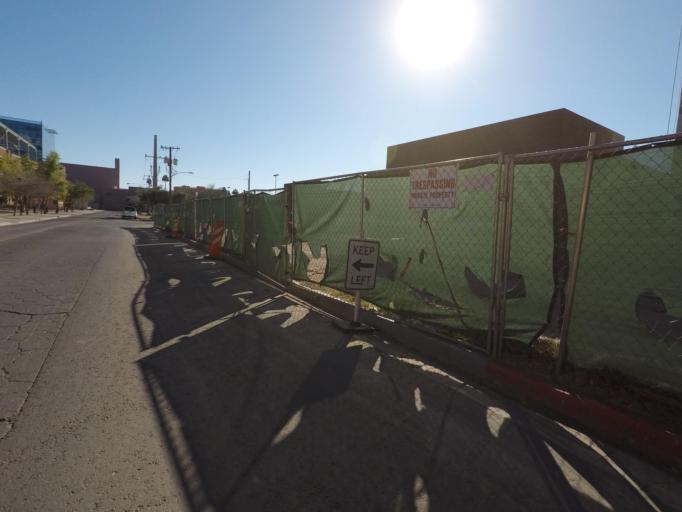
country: US
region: Arizona
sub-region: Maricopa County
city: Tempe Junction
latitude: 33.4209
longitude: -111.9382
